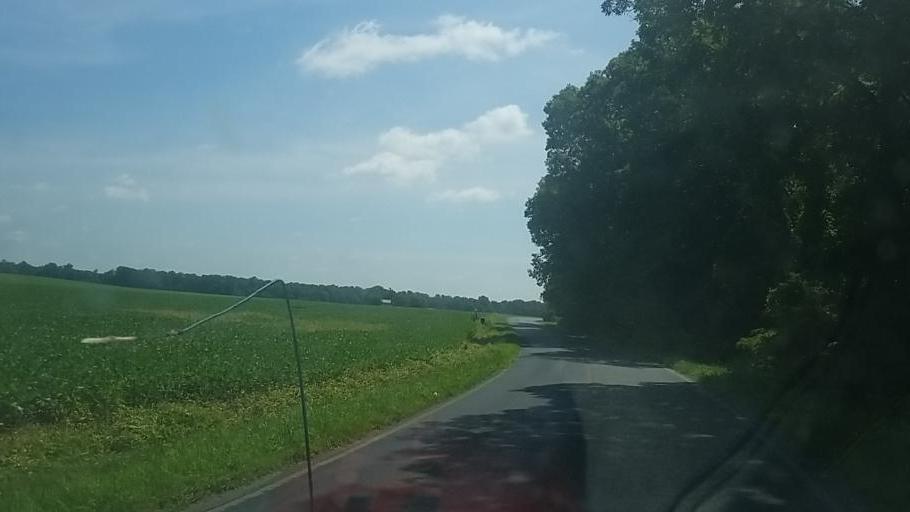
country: US
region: Maryland
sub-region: Caroline County
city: Ridgely
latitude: 38.8924
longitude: -75.9312
